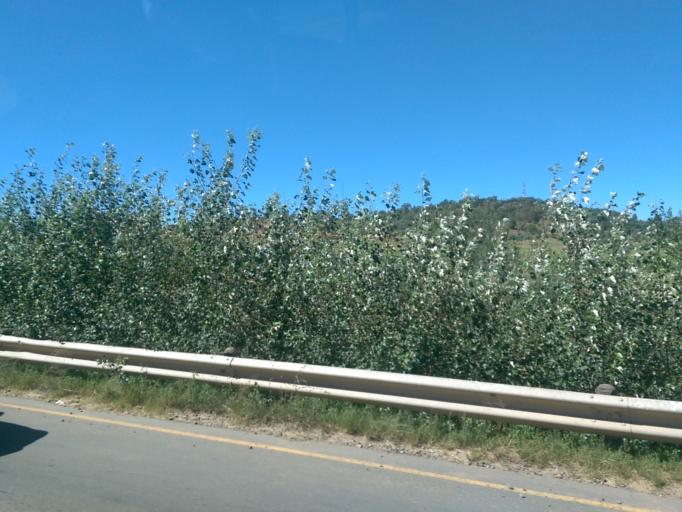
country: LS
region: Maseru
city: Maseru
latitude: -29.3994
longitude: 27.5547
